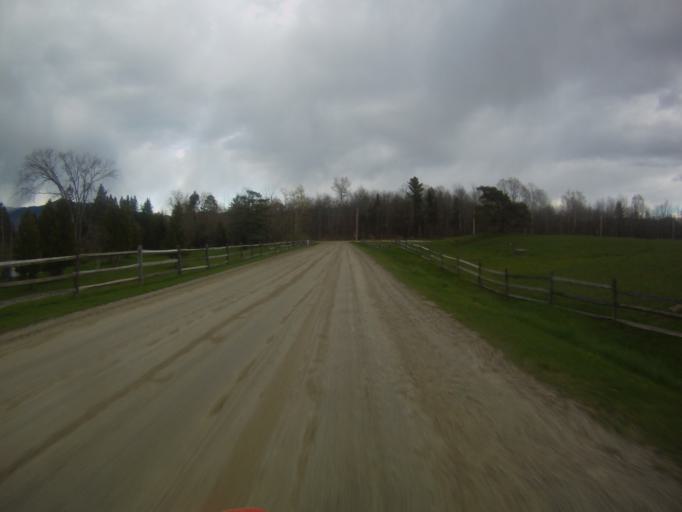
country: US
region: Vermont
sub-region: Addison County
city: Bristol
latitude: 44.0601
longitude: -73.0091
